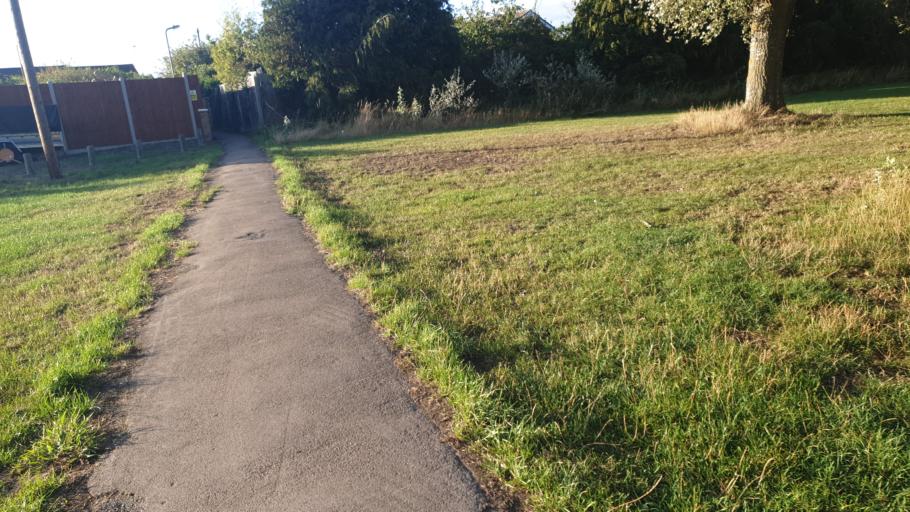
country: GB
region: England
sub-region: Essex
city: Clacton-on-Sea
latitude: 51.8058
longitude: 1.1787
